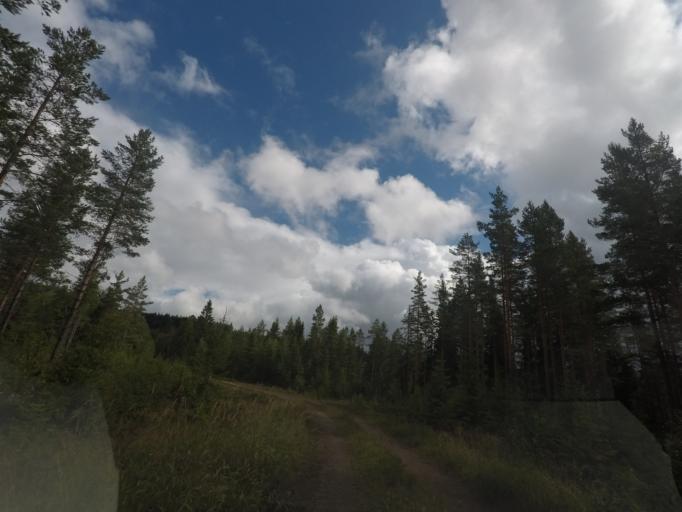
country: SE
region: Vaermland
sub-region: Filipstads Kommun
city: Lesjofors
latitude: 60.1047
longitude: 14.3887
